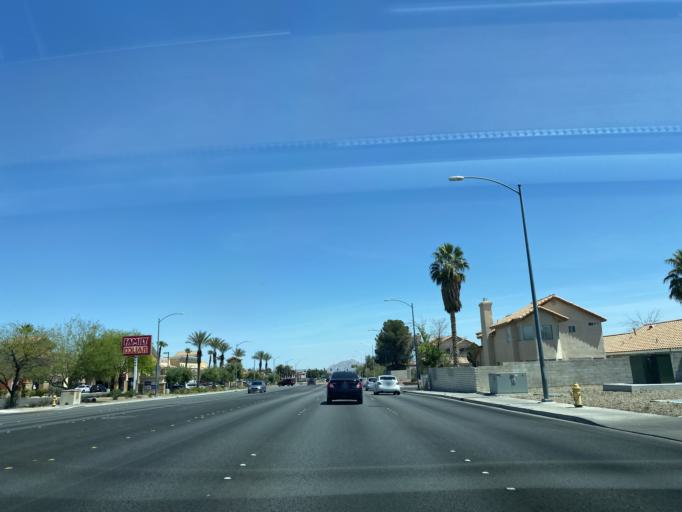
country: US
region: Nevada
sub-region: Clark County
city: Spring Valley
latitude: 36.1959
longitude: -115.2364
